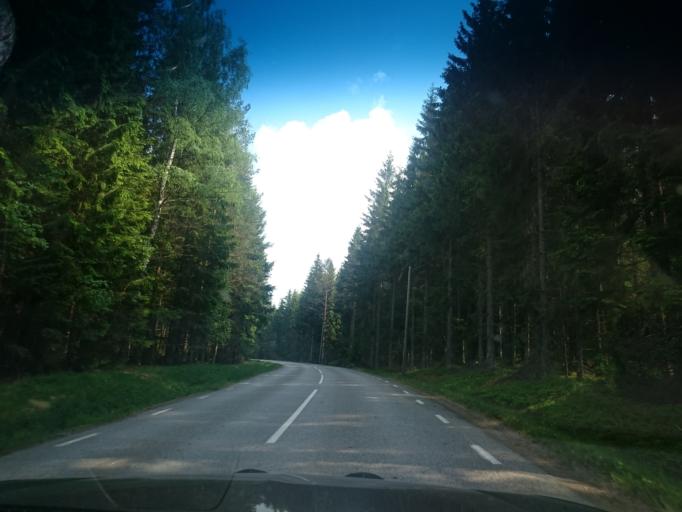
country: SE
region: Joenkoeping
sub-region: Vetlanda Kommun
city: Vetlanda
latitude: 57.3357
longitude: 15.0766
